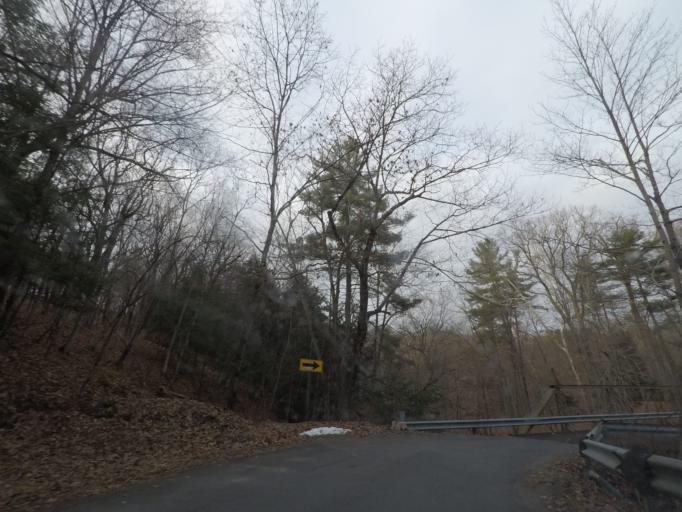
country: US
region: New York
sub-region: Rensselaer County
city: Wynantskill
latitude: 42.7241
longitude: -73.6471
